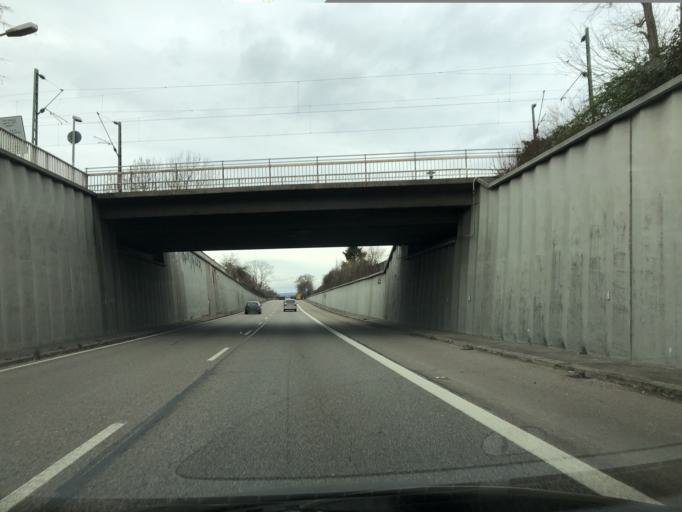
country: DE
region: Baden-Wuerttemberg
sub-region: Freiburg Region
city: Freiburg
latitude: 47.9981
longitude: 7.8222
